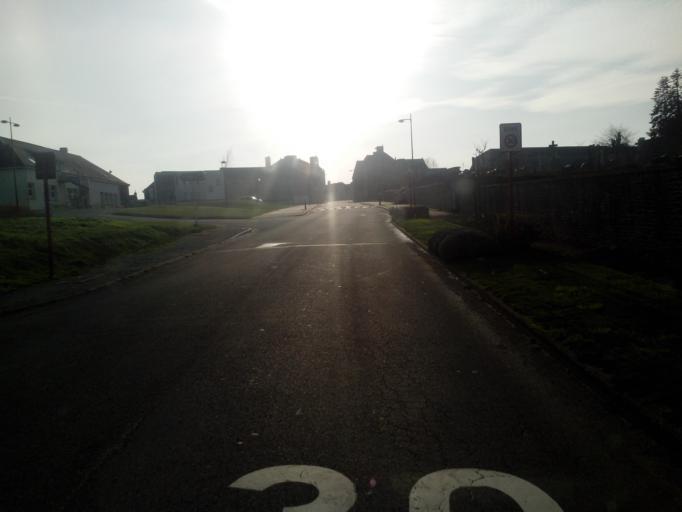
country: FR
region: Brittany
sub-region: Departement du Morbihan
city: Mauron
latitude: 48.0853
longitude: -2.2830
